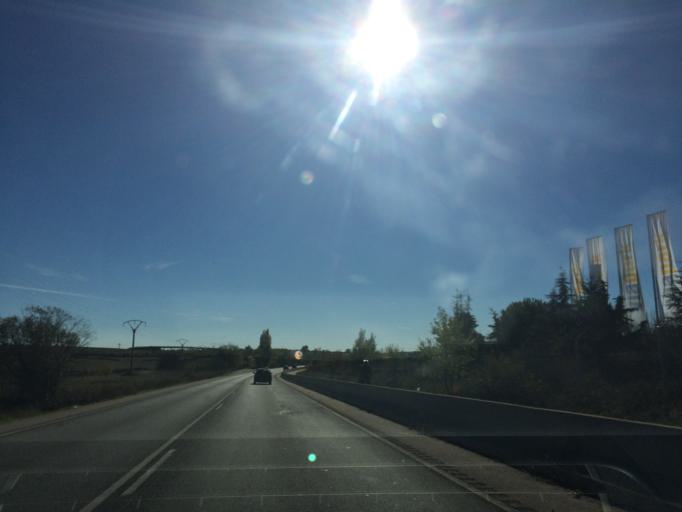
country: ES
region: Madrid
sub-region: Provincia de Madrid
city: Manzanares el Real
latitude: 40.7290
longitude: -3.7905
